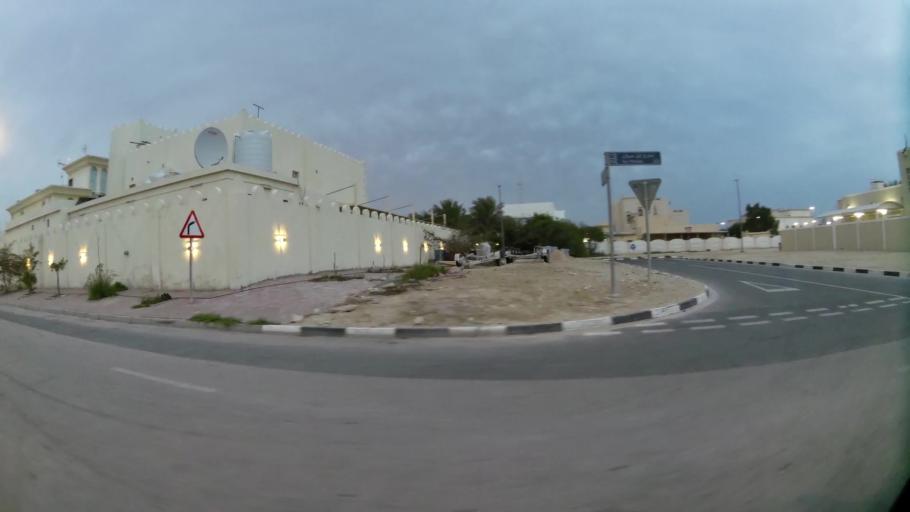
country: QA
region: Baladiyat ad Dawhah
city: Doha
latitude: 25.3458
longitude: 51.5117
